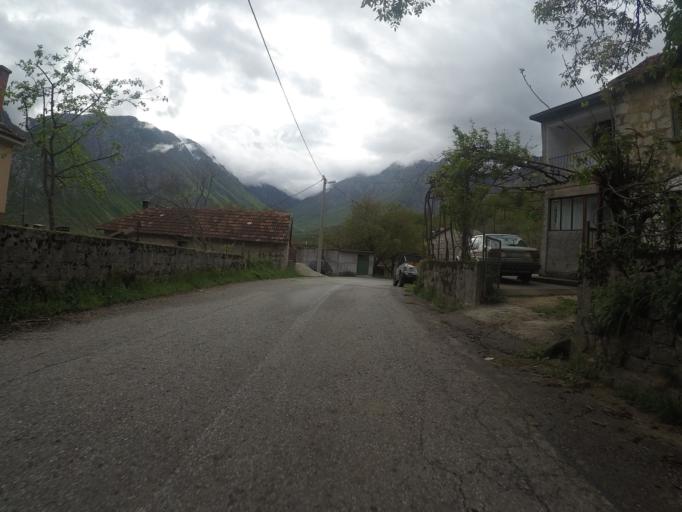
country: BA
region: Federation of Bosnia and Herzegovina
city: Siroki Brijeg
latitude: 43.5409
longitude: 17.5837
